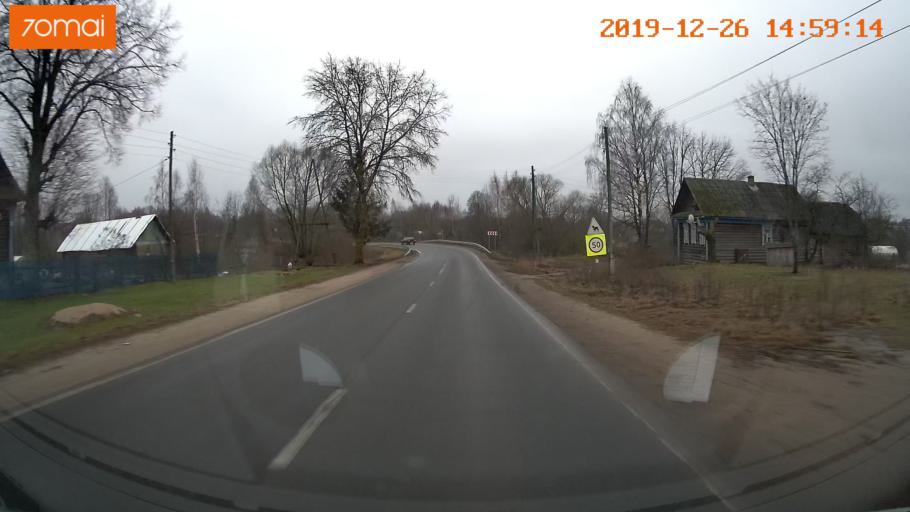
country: RU
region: Jaroslavl
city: Rybinsk
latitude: 58.2608
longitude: 38.8479
